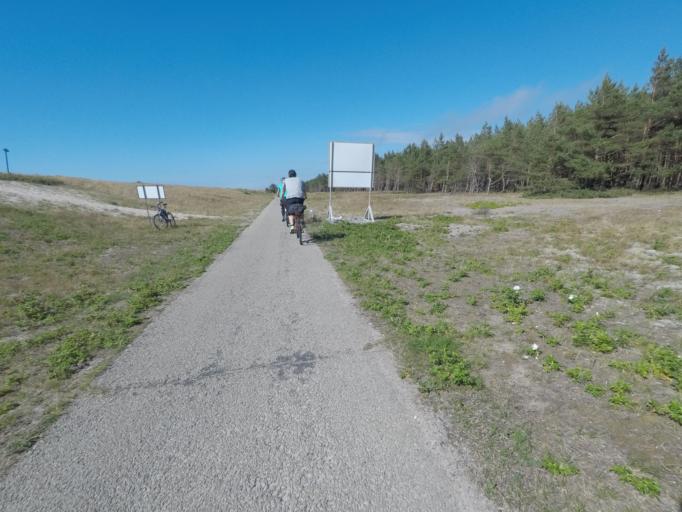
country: LT
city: Neringa
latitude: 55.5164
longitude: 21.0940
